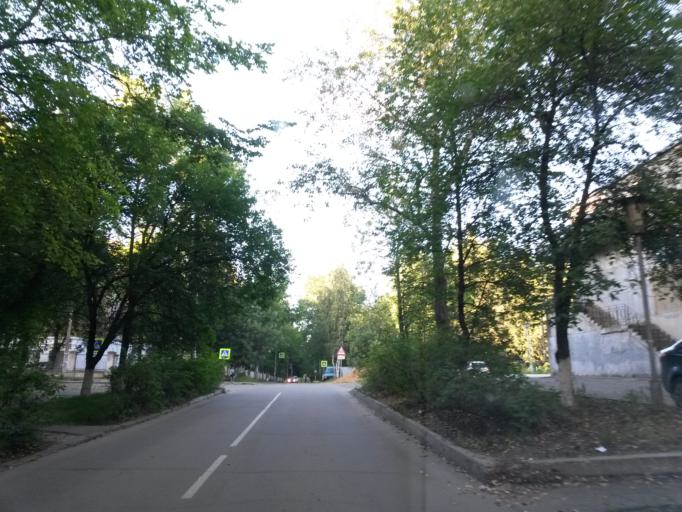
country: RU
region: Jaroslavl
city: Yaroslavl
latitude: 57.5802
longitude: 39.8459
